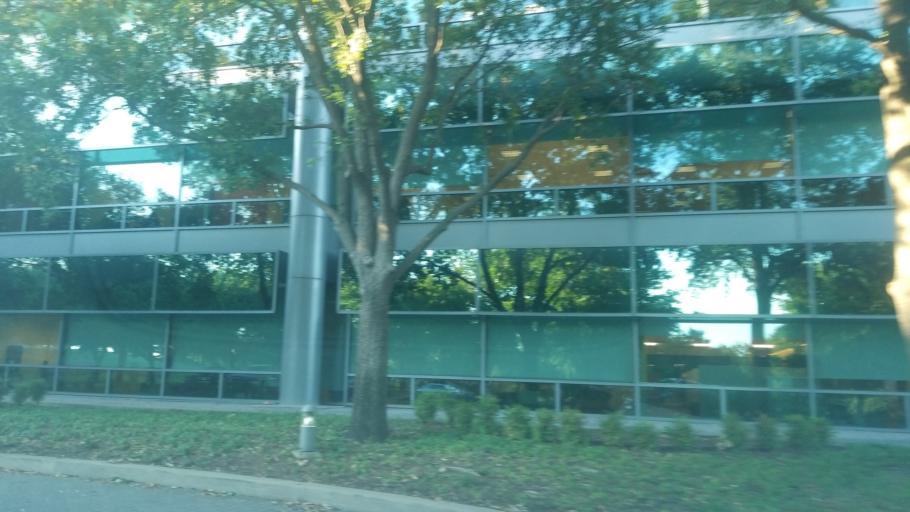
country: US
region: Texas
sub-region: Dallas County
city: Irving
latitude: 32.8757
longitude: -96.9537
